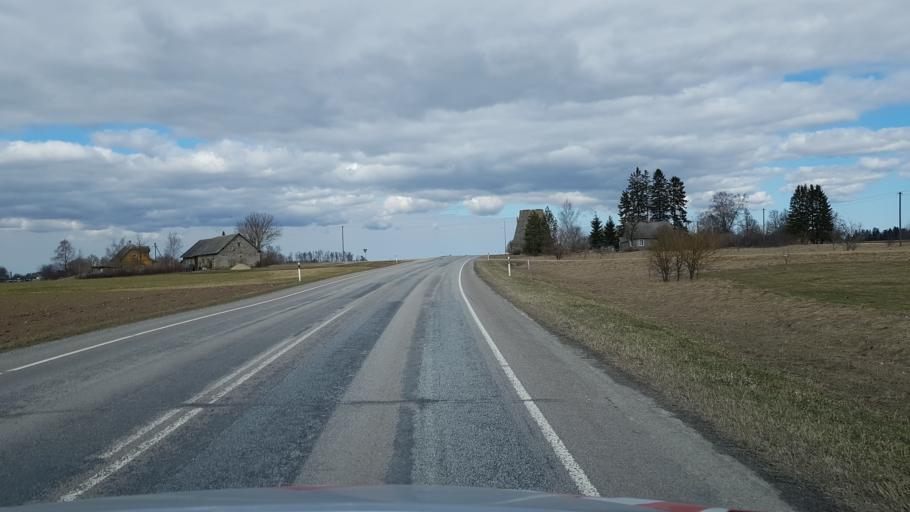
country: EE
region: Laeaene-Virumaa
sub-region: Vaeike-Maarja vald
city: Vaike-Maarja
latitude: 59.1579
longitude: 26.2637
